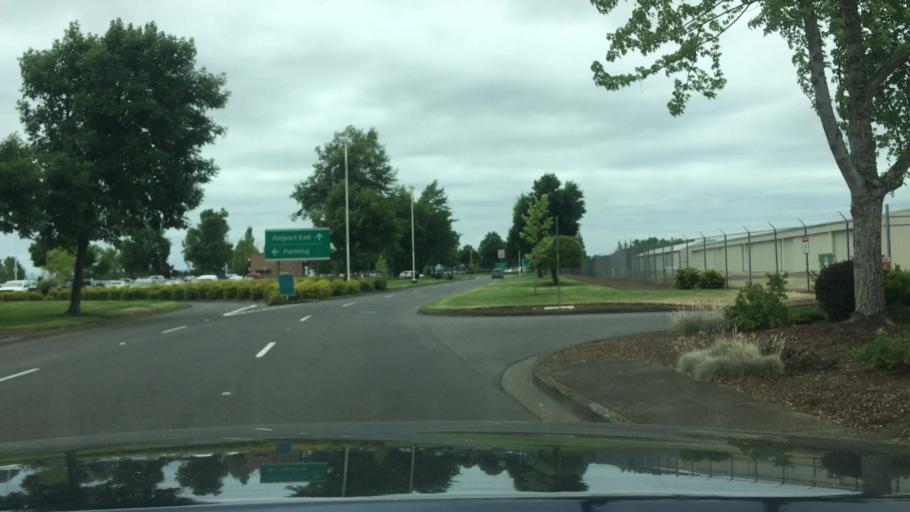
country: US
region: Oregon
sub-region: Lane County
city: Junction City
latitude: 44.1178
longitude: -123.2121
